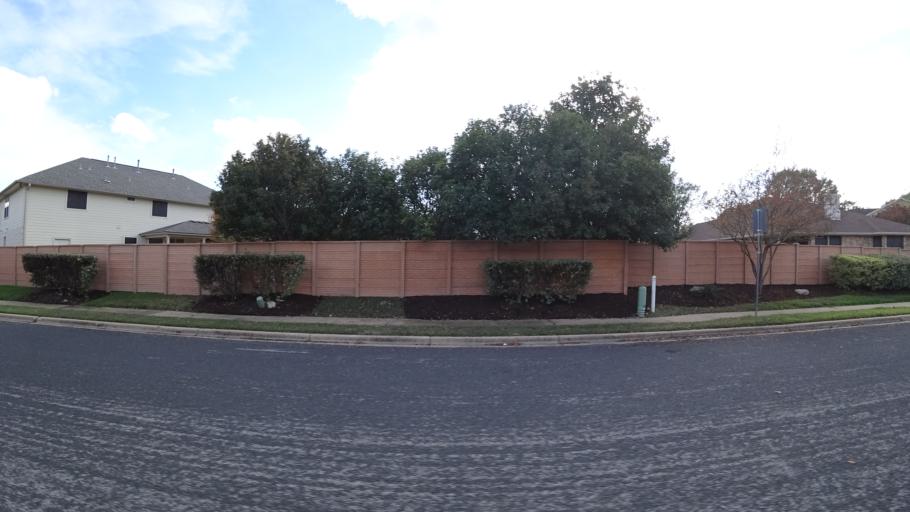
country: US
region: Texas
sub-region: Williamson County
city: Brushy Creek
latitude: 30.5092
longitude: -97.7360
